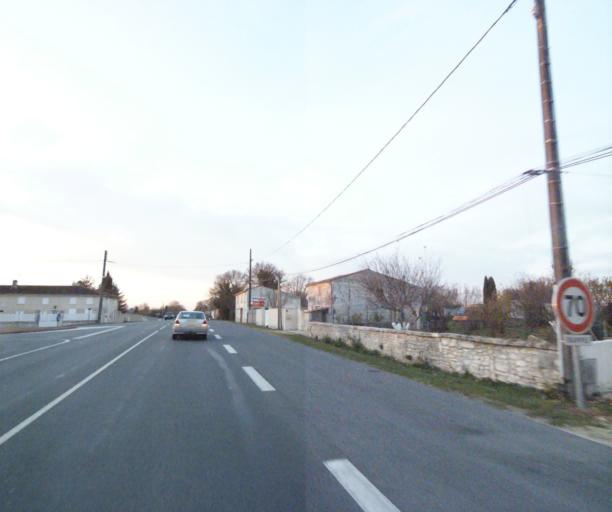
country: FR
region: Poitou-Charentes
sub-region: Departement de la Charente-Maritime
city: Saint-Georges-des-Coteaux
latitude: 45.7866
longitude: -0.7176
